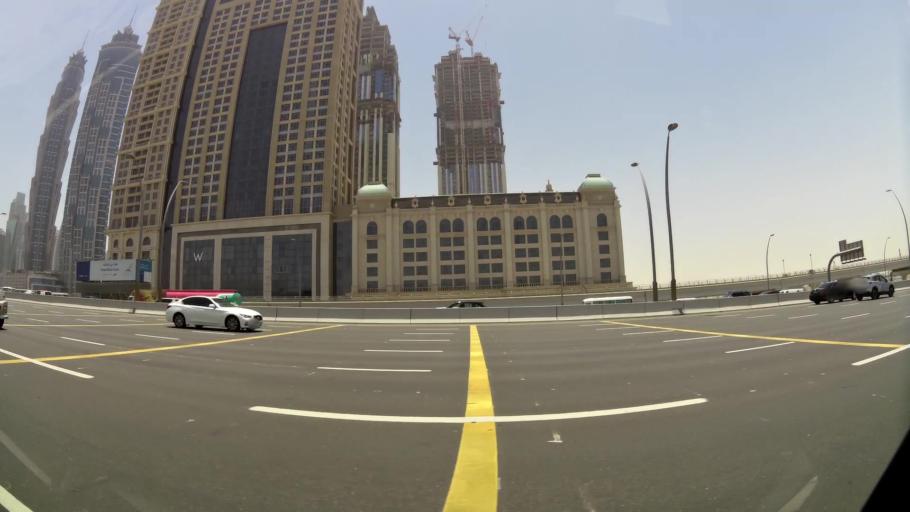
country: AE
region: Dubai
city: Dubai
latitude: 25.1846
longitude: 55.2531
